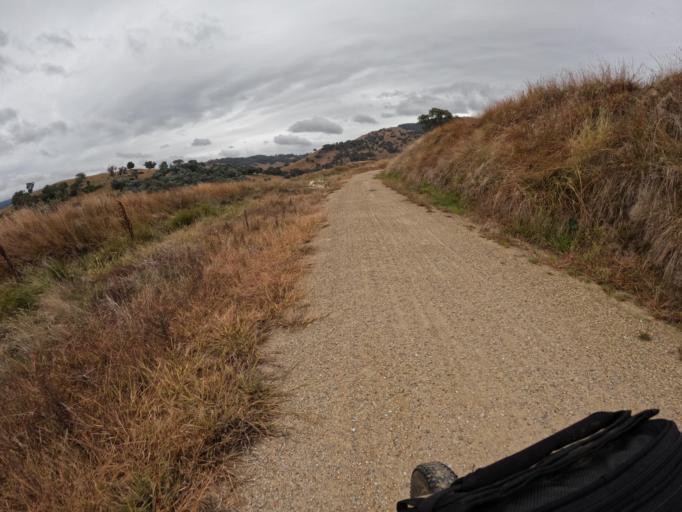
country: AU
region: New South Wales
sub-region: Albury Municipality
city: East Albury
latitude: -36.1807
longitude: 147.3754
